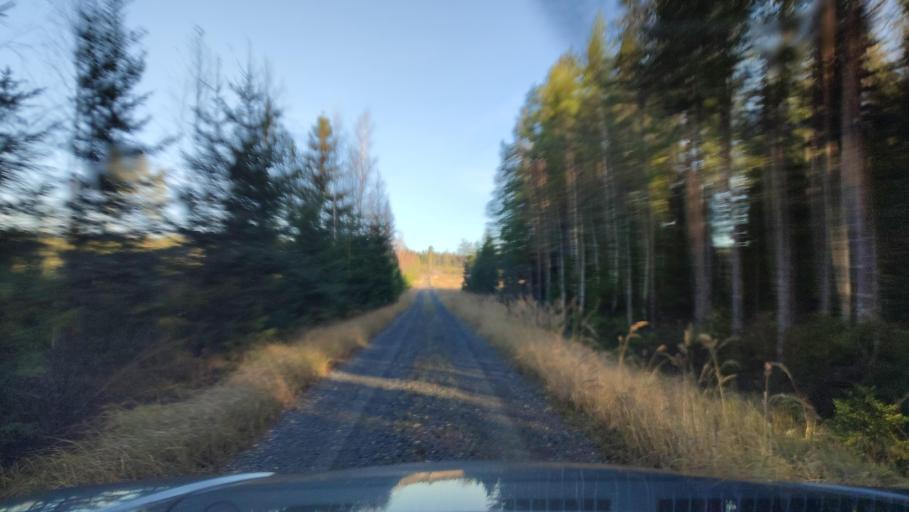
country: FI
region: Southern Ostrobothnia
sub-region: Suupohja
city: Karijoki
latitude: 62.1987
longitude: 21.6129
